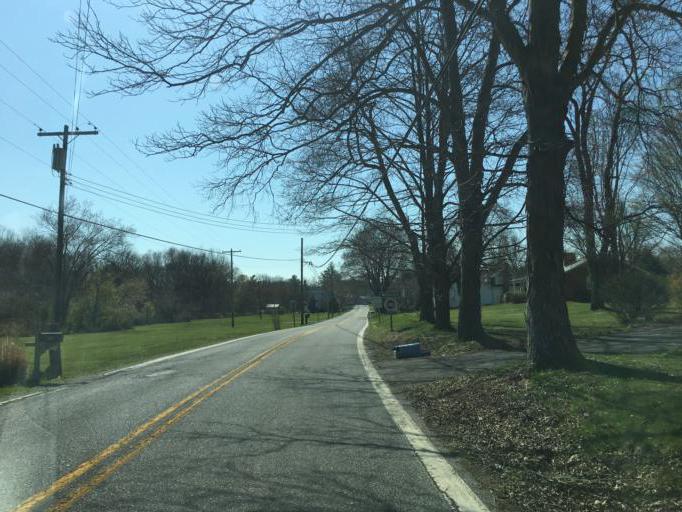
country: US
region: Maryland
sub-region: Frederick County
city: Myersville
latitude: 39.5773
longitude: -77.5544
